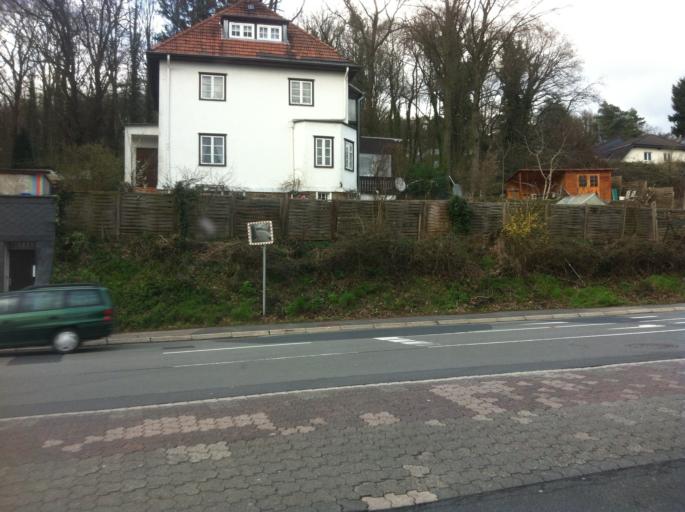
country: DE
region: North Rhine-Westphalia
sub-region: Regierungsbezirk Koln
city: Bergisch Gladbach
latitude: 50.9584
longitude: 7.1703
